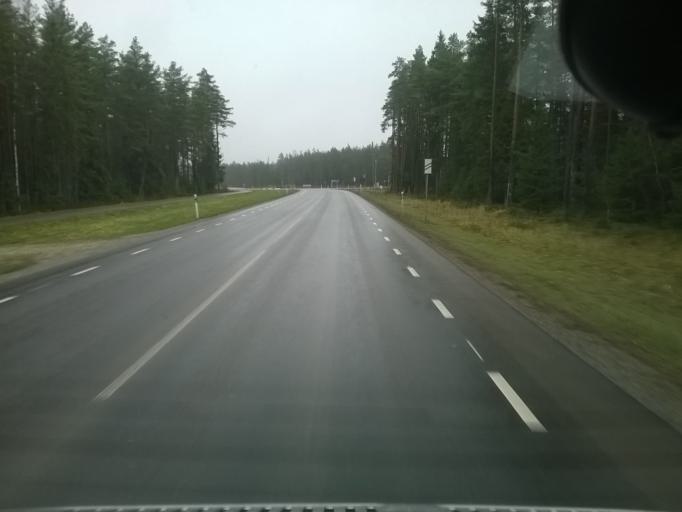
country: EE
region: Harju
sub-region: Saku vald
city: Saku
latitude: 59.2497
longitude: 24.6853
